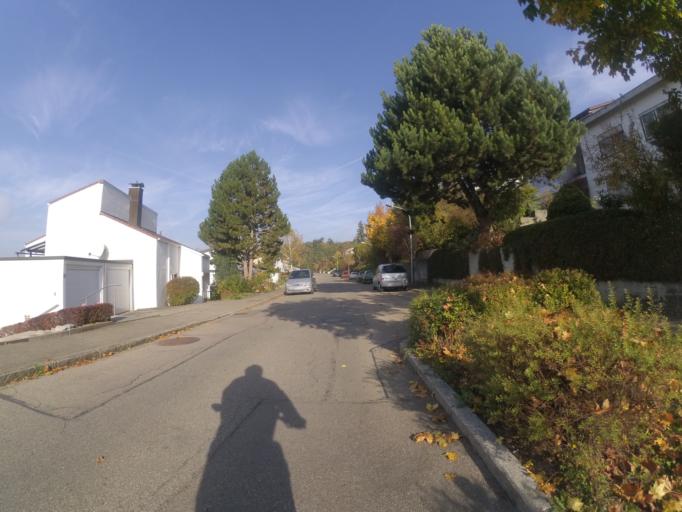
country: DE
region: Baden-Wuerttemberg
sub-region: Tuebingen Region
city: Dornstadt
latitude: 48.4168
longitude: 9.9256
